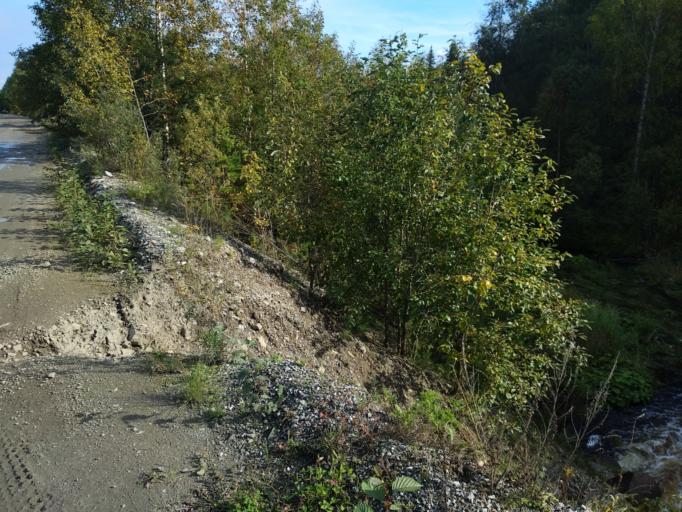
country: RU
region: Sverdlovsk
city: Karpinsk
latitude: 59.8059
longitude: 59.9109
